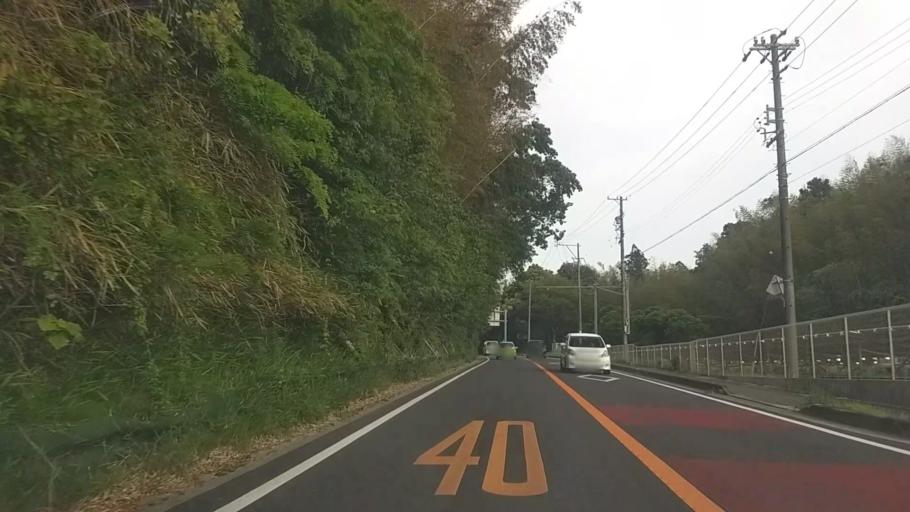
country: JP
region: Shizuoka
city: Hamamatsu
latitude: 34.7612
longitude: 137.6628
